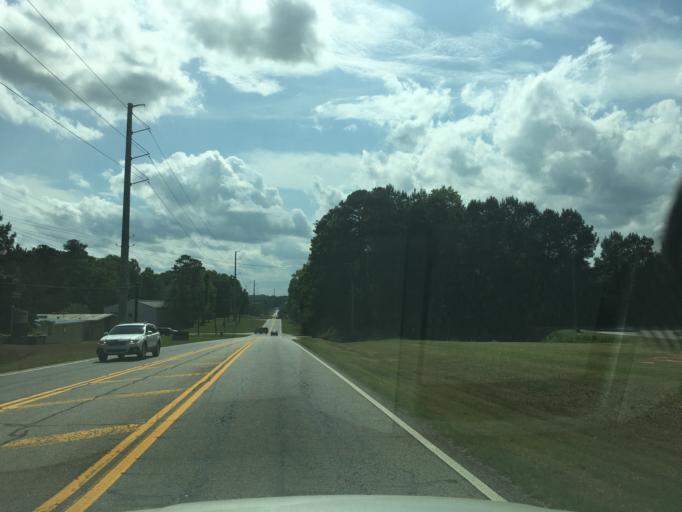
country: US
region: Georgia
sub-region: Jackson County
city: Braselton
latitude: 34.1031
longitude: -83.7843
